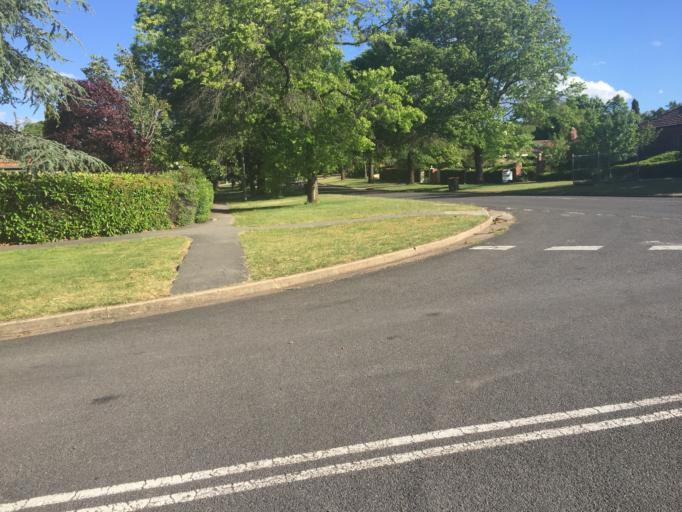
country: AU
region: Australian Capital Territory
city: Forrest
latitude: -35.3240
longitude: 149.1382
